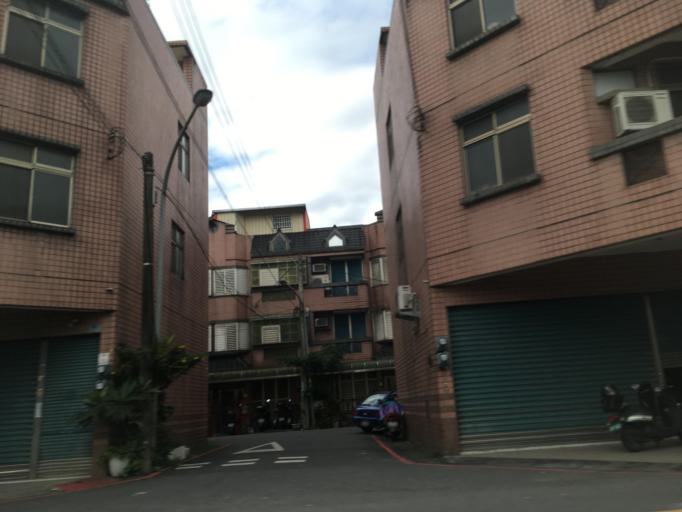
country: TW
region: Taiwan
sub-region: Yilan
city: Yilan
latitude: 24.6950
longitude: 121.7317
